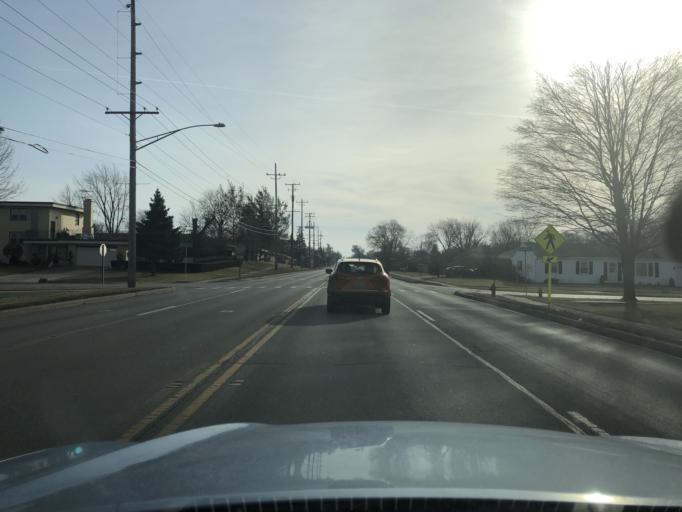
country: US
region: Illinois
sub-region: DuPage County
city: Roselle
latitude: 41.9892
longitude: -88.0803
